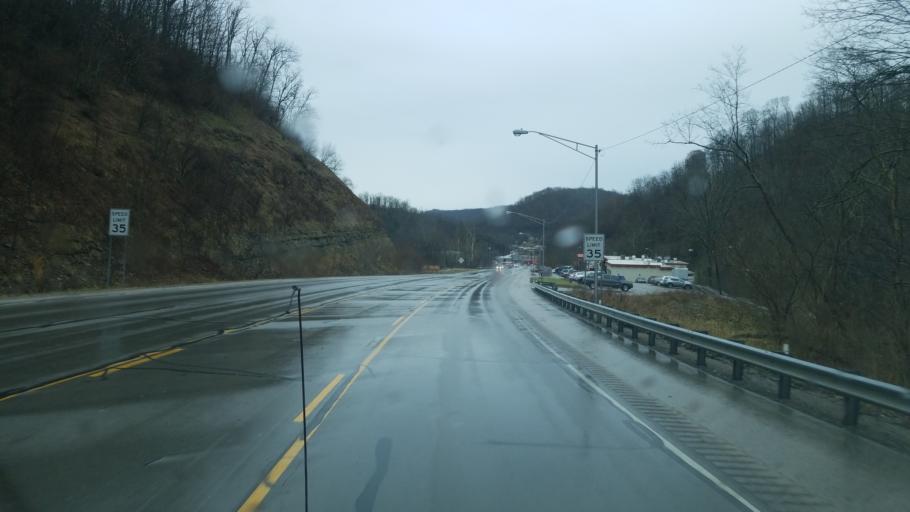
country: US
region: Ohio
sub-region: Brown County
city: Aberdeen
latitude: 38.6405
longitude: -83.7663
